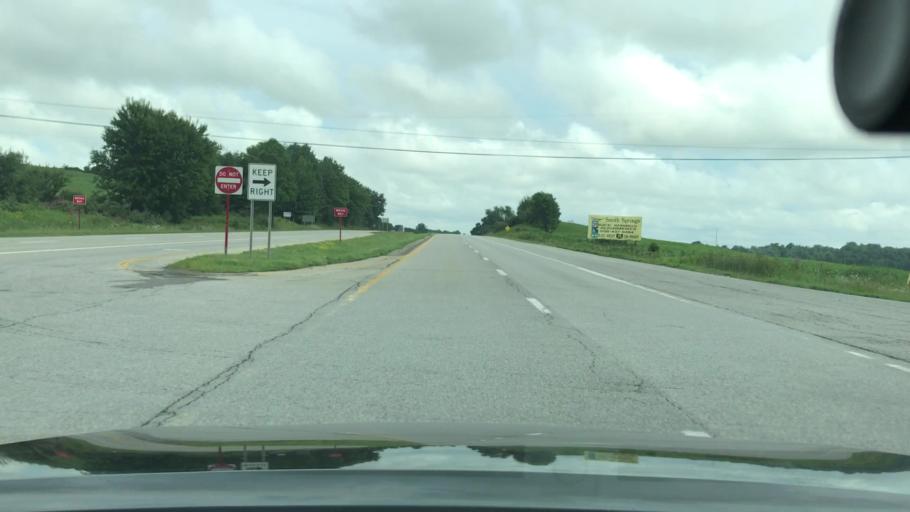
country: US
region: Ohio
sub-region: Jackson County
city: Jackson
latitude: 38.9988
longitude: -82.5534
